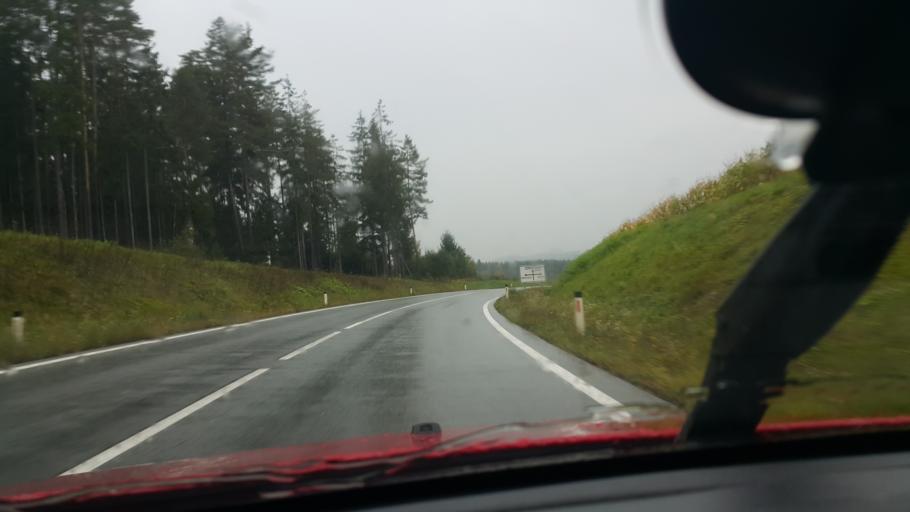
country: AT
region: Carinthia
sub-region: Politischer Bezirk Volkermarkt
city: Ruden
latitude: 46.6566
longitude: 14.7624
